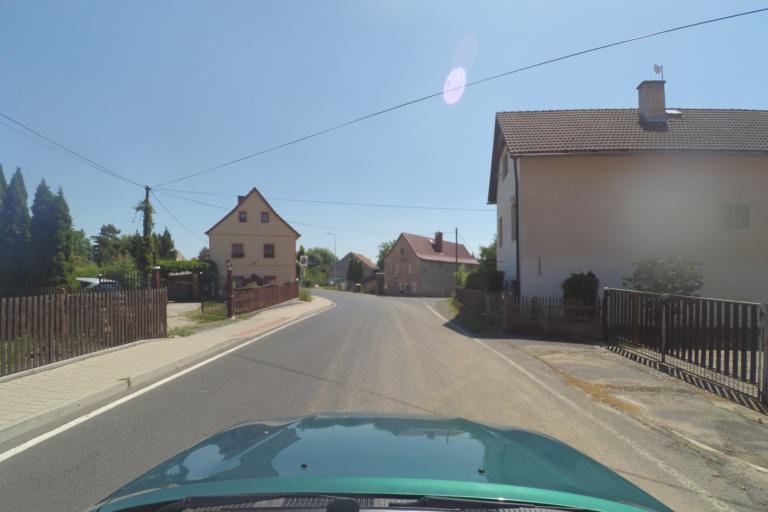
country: CZ
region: Ustecky
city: Chlumec
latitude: 50.6933
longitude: 13.9227
